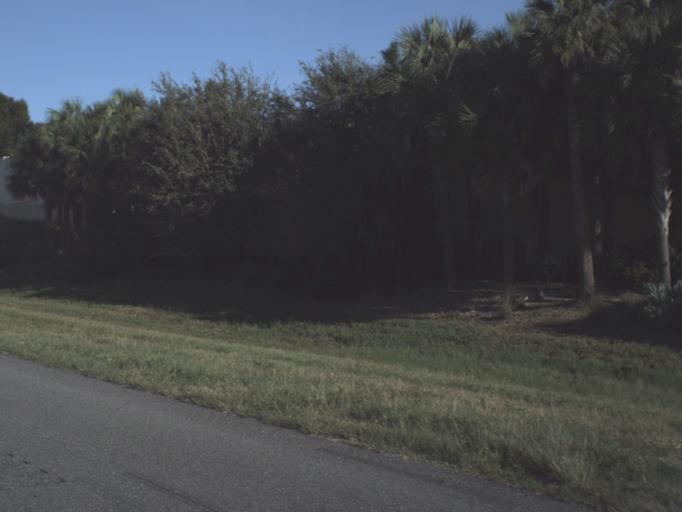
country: US
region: Florida
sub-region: Orange County
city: Gotha
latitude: 28.5246
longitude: -81.5124
